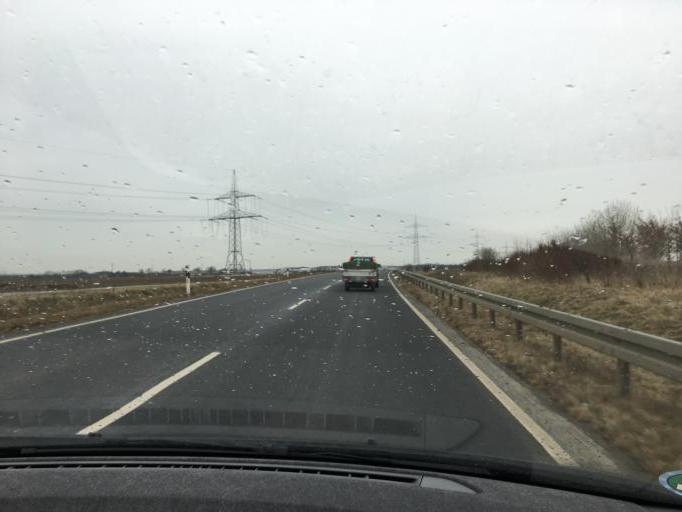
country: DE
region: North Rhine-Westphalia
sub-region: Regierungsbezirk Koln
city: Bergheim
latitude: 50.9005
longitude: 6.6322
